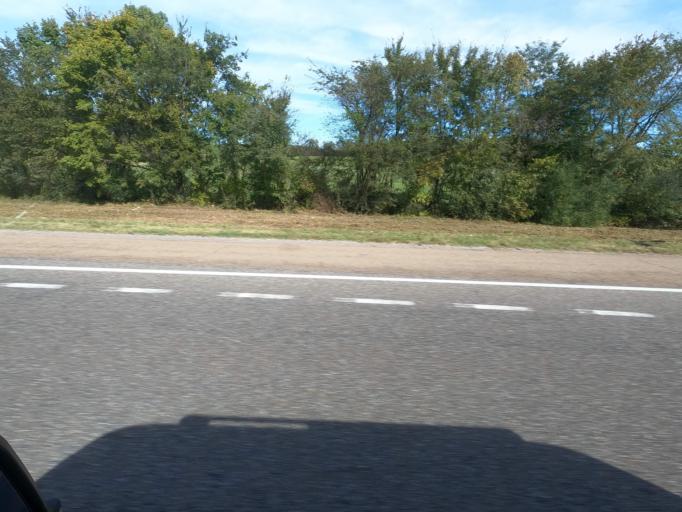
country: US
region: Tennessee
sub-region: Humphreys County
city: Waverly
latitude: 35.8813
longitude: -87.8073
